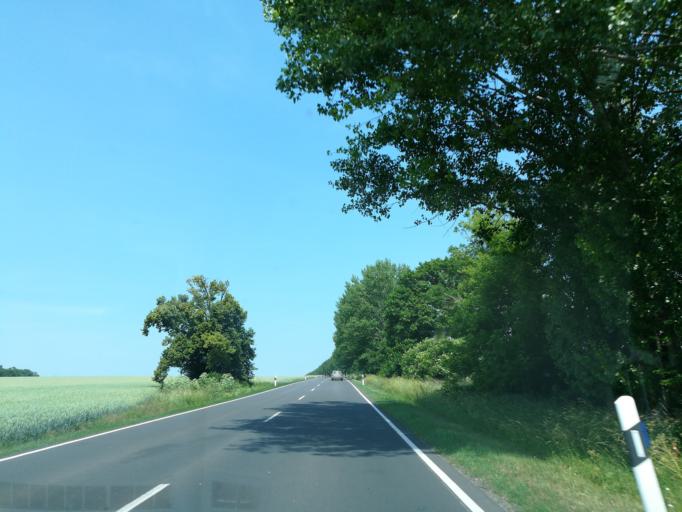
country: DE
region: Saxony-Anhalt
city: Gross Bornecke
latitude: 51.8313
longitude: 11.4565
